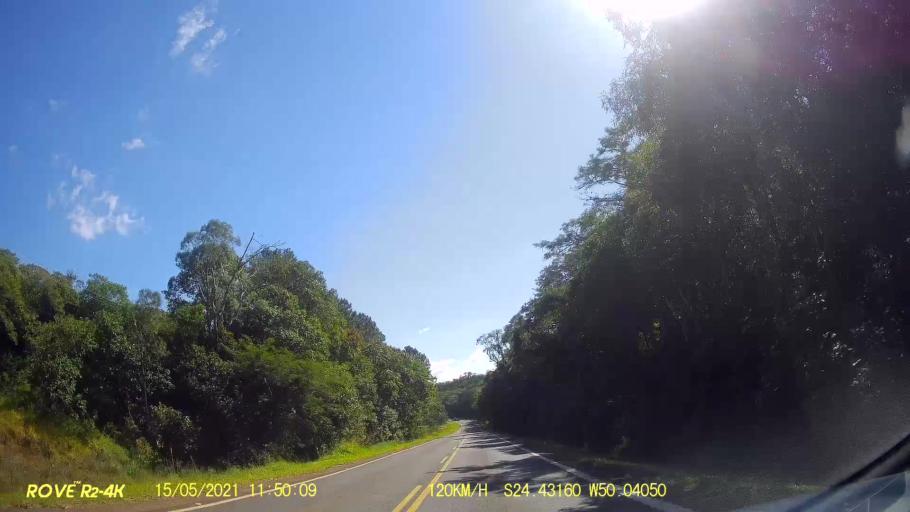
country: BR
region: Parana
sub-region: Pirai Do Sul
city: Pirai do Sul
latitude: -24.4318
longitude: -50.0404
